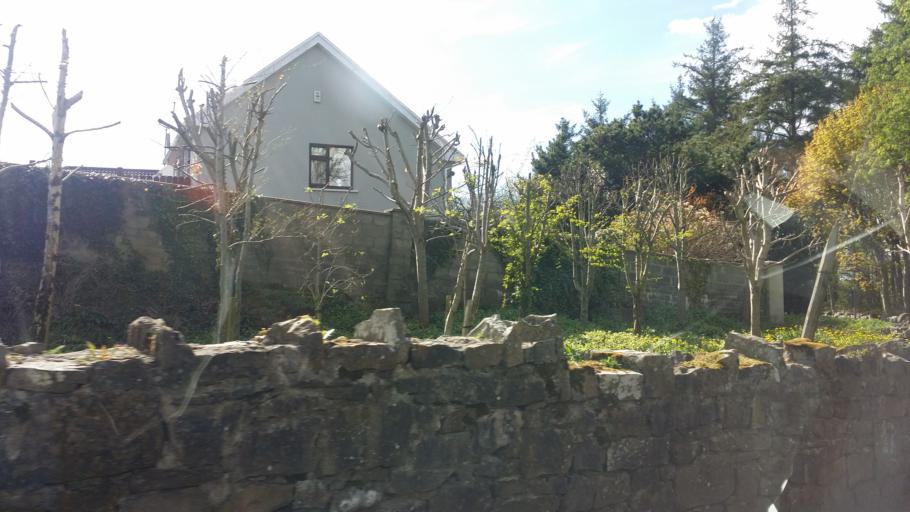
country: IE
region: Ulster
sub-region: County Donegal
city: Ballyshannon
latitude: 54.5046
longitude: -8.1973
